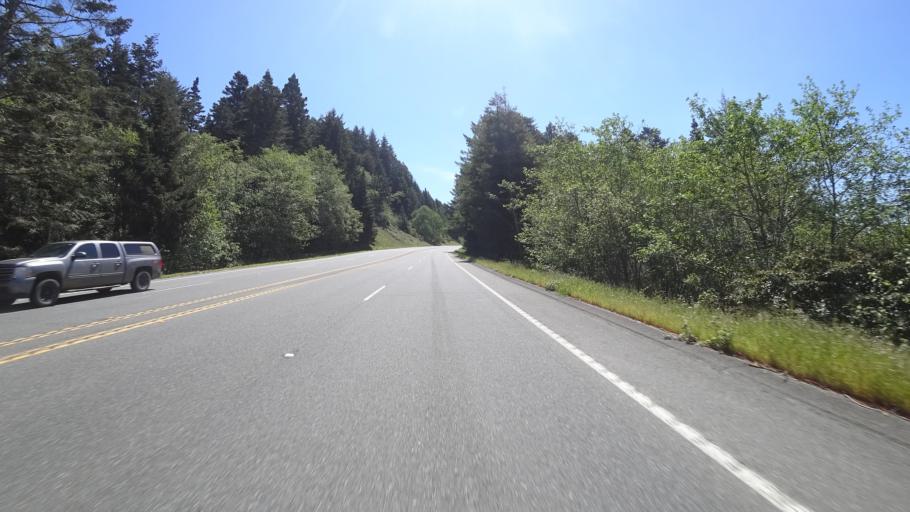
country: US
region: California
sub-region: Humboldt County
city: Westhaven-Moonstone
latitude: 41.0444
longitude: -124.1169
